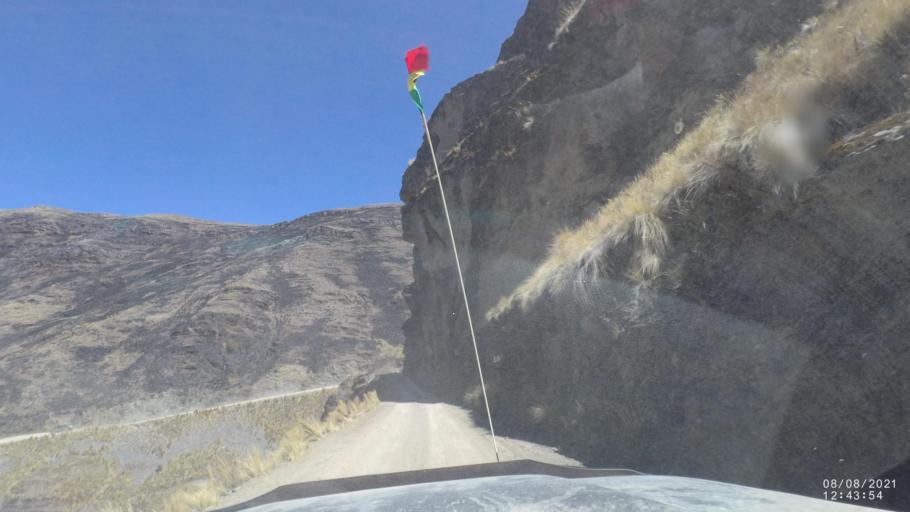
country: BO
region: Cochabamba
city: Colchani
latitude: -16.8441
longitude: -66.6113
